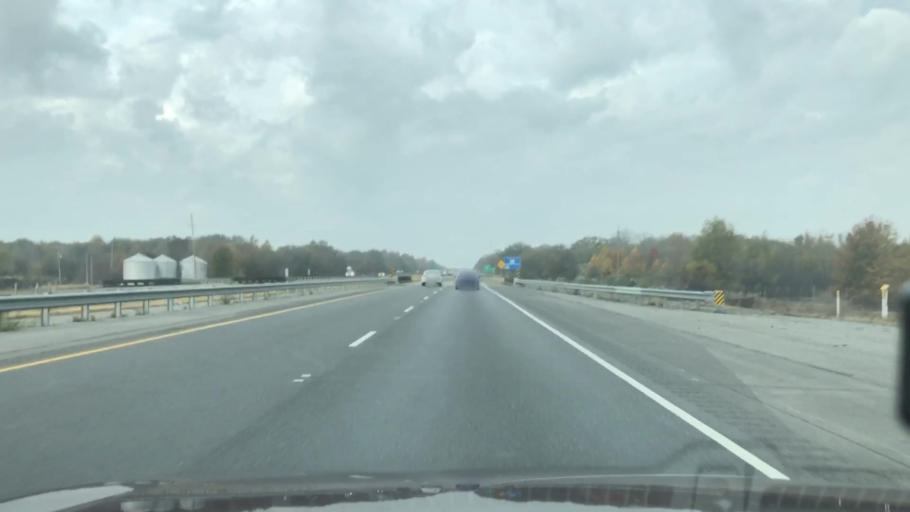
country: US
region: Louisiana
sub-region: Richland Parish
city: Delhi
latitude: 32.4388
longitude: -91.4671
